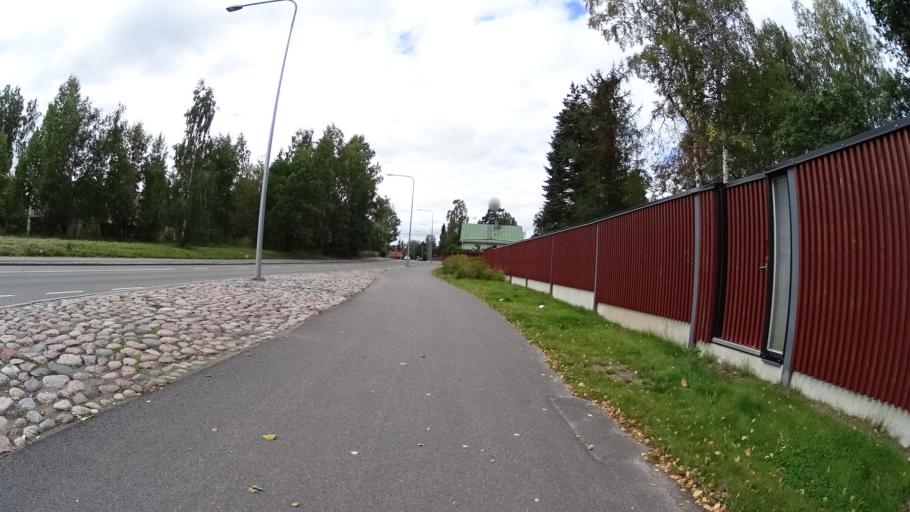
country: FI
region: Uusimaa
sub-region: Helsinki
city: Vantaa
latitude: 60.2697
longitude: 25.0235
